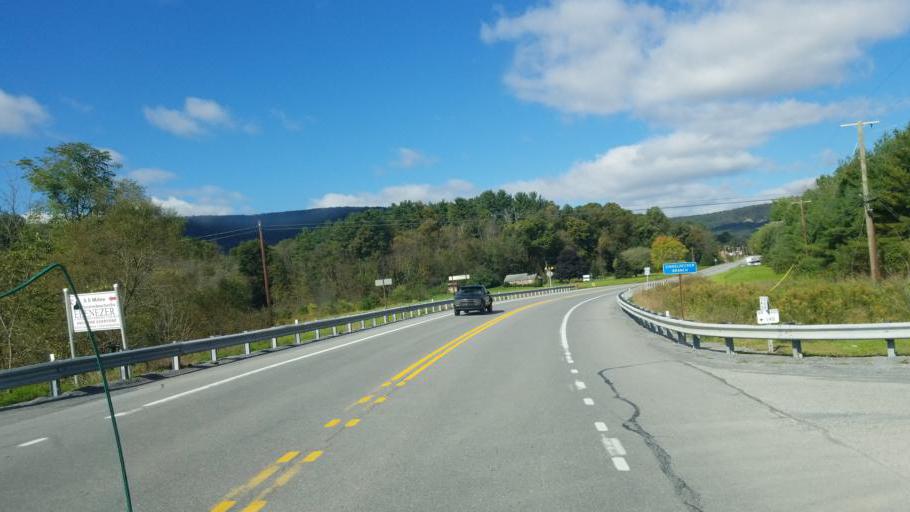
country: US
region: Pennsylvania
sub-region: Fulton County
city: McConnellsburg
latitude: 39.9978
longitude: -78.0975
